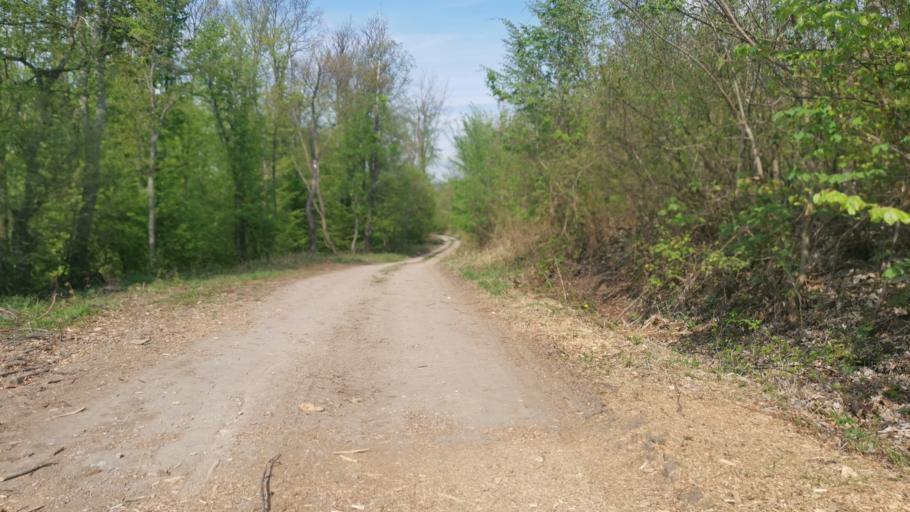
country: SK
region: Trnavsky
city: Smolenice
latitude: 48.5661
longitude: 17.3584
